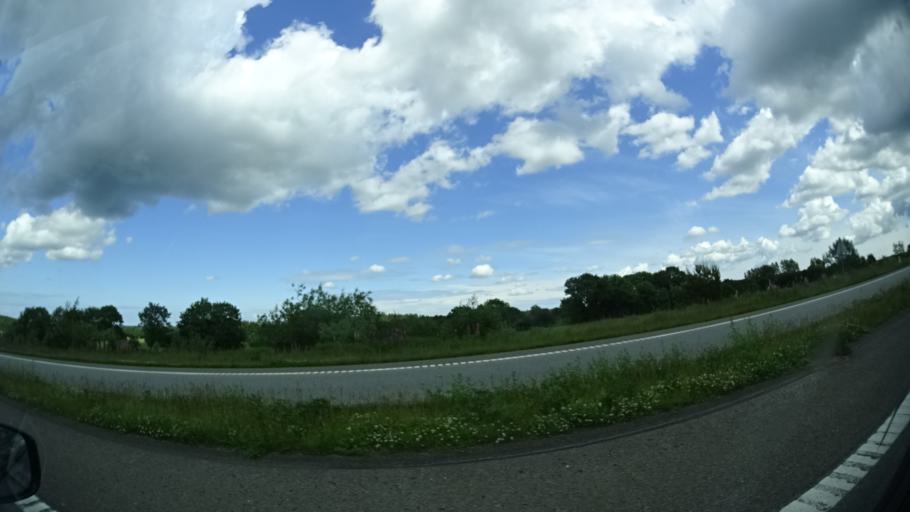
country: DK
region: Central Jutland
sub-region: Syddjurs Kommune
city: Ronde
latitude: 56.3051
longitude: 10.5049
